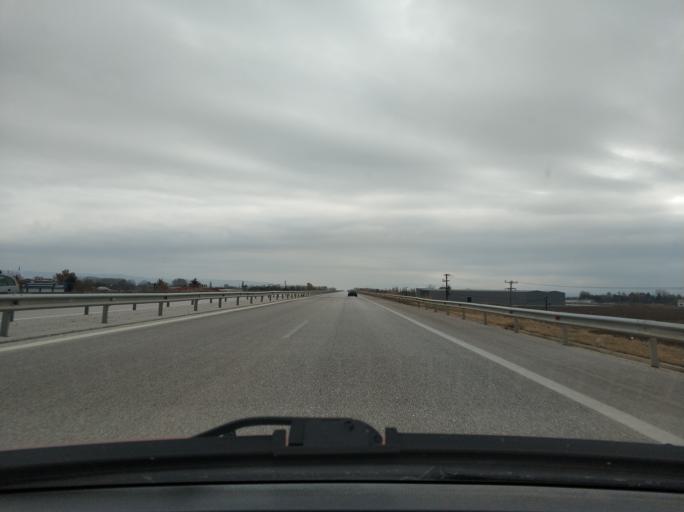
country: GR
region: Central Macedonia
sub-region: Nomos Thessalonikis
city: Kavallari
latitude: 40.7355
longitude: 23.0359
